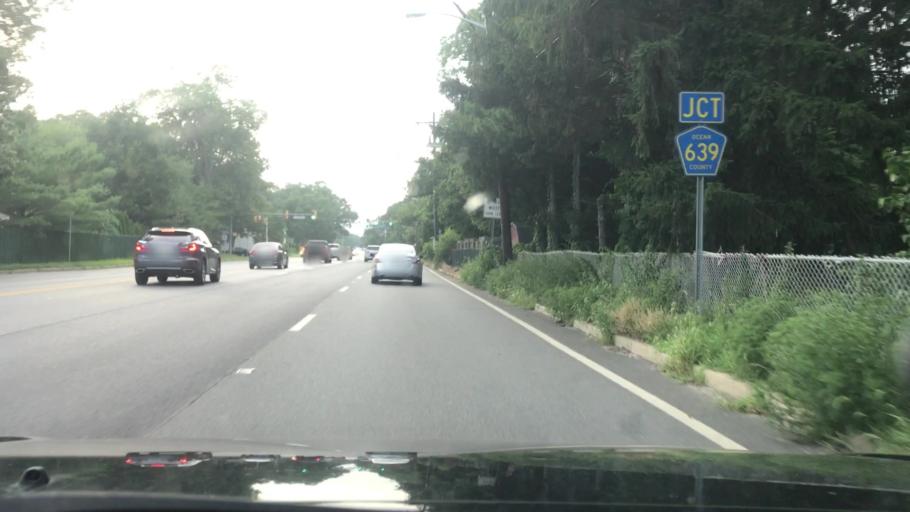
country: US
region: New Jersey
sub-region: Ocean County
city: Lakewood
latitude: 40.1102
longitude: -74.2379
